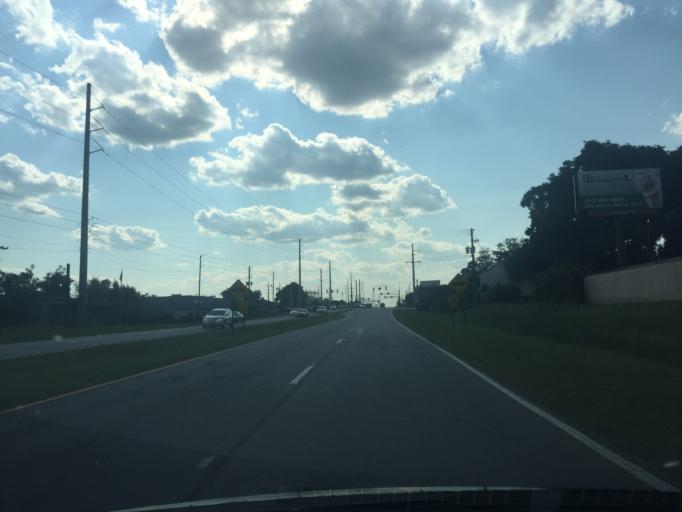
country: US
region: Georgia
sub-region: Chatham County
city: Thunderbolt
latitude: 32.0662
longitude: -81.0424
